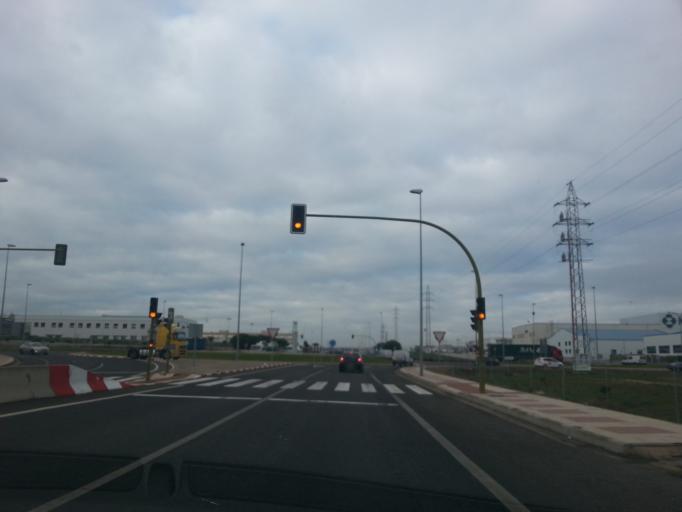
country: ES
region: Castille and Leon
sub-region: Provincia de Salamanca
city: Carbajosa de la Sagrada
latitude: 40.9427
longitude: -5.6543
